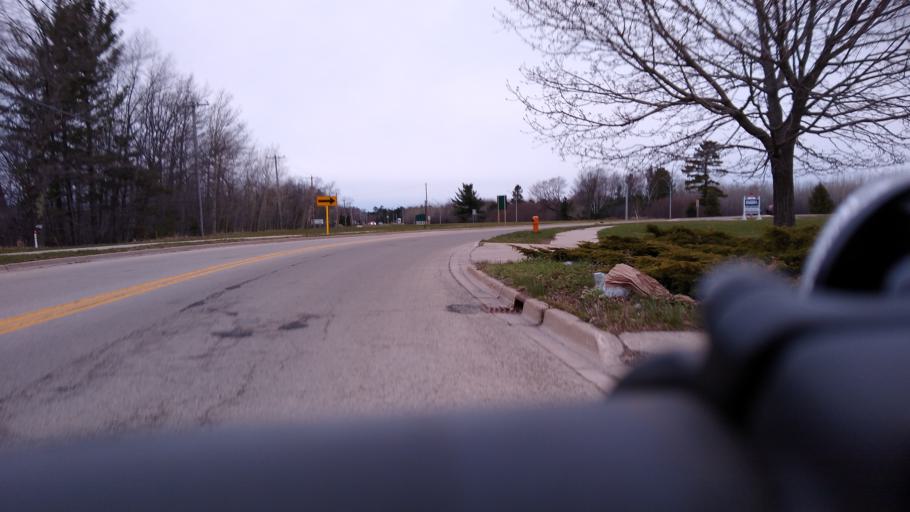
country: US
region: Michigan
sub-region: Delta County
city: Escanaba
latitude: 45.7155
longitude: -87.0796
